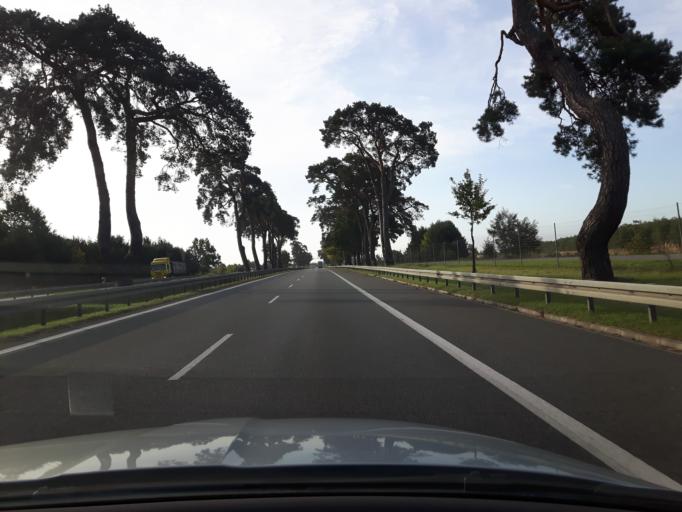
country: PL
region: Masovian Voivodeship
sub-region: Powiat bialobrzeski
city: Stara Blotnica
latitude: 51.5933
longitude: 20.9933
